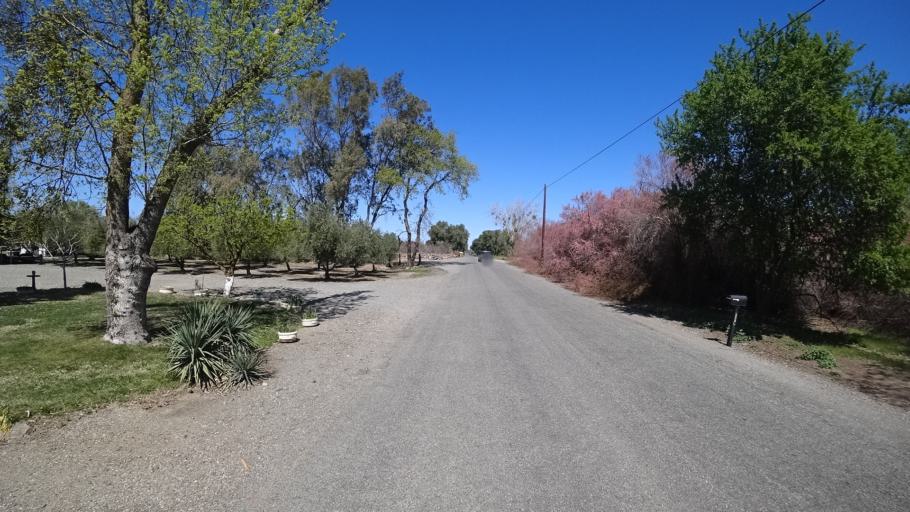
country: US
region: California
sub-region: Glenn County
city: Orland
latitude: 39.7700
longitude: -122.2387
